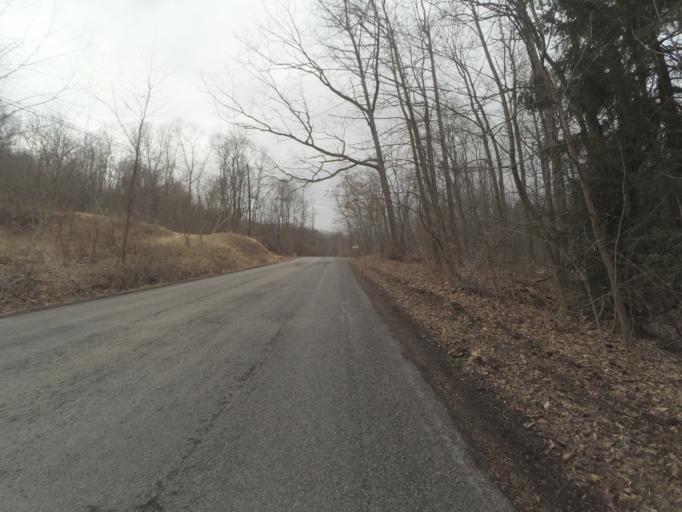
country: US
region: Pennsylvania
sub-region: Centre County
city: Stormstown
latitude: 40.8689
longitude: -78.0084
